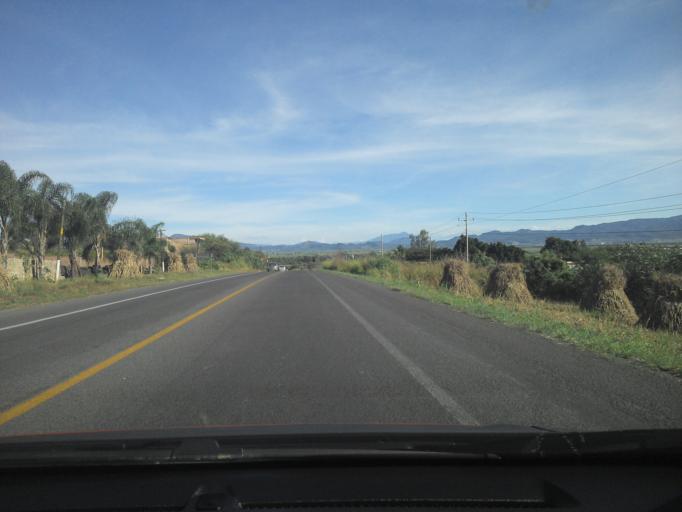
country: MX
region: Jalisco
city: Teuchitlan
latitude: 20.6785
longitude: -103.8386
